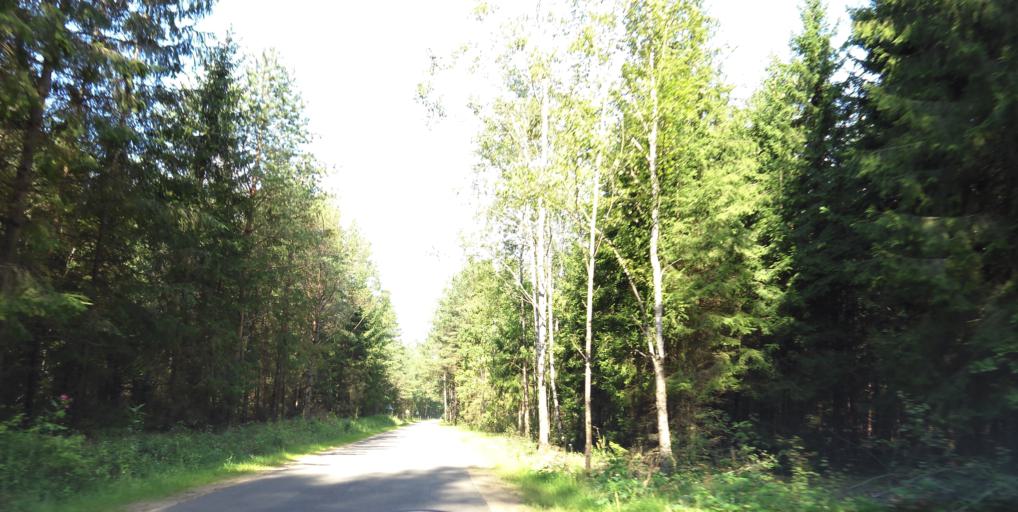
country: LT
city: Grigiskes
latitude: 54.7246
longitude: 25.0517
